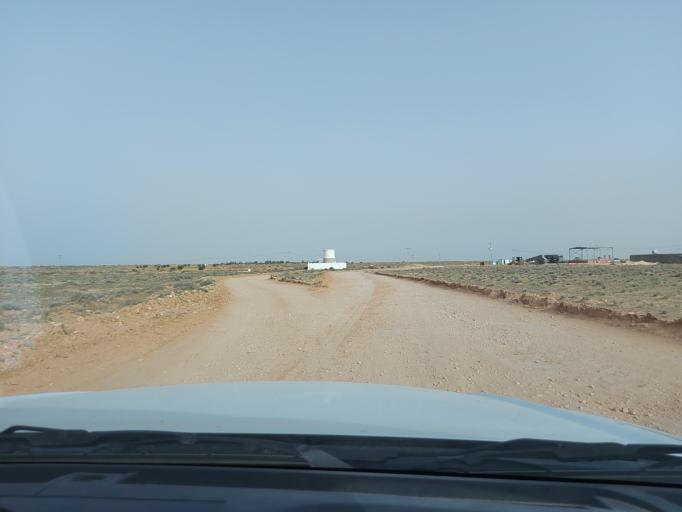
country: TN
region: Madanin
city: Medenine
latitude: 33.2651
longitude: 10.5706
